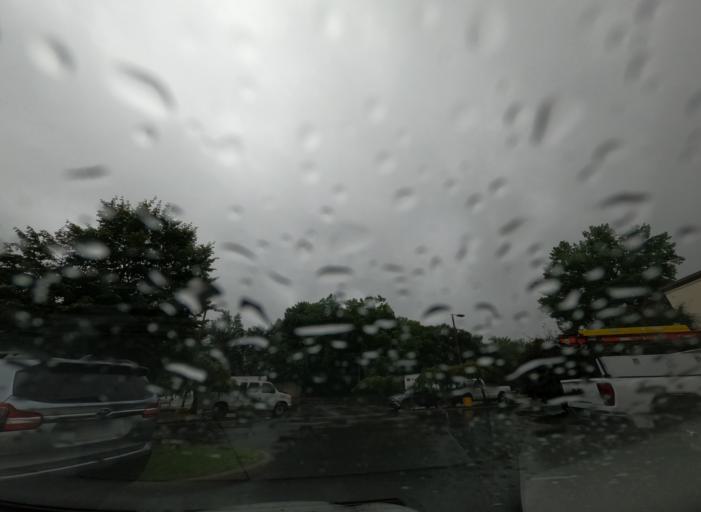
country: US
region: Kentucky
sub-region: Jefferson County
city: Hurstbourne Acres
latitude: 38.2158
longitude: -85.5759
